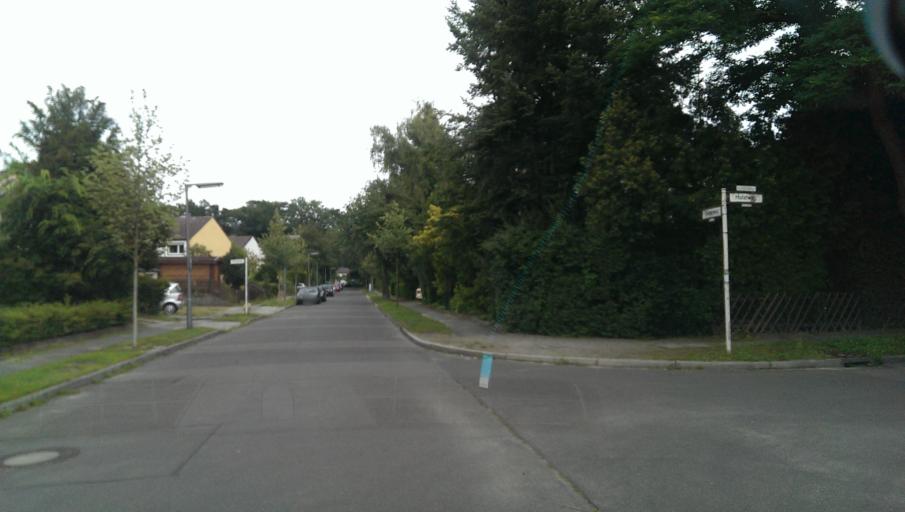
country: DE
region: Berlin
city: Zehlendorf Bezirk
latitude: 52.4308
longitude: 13.2333
